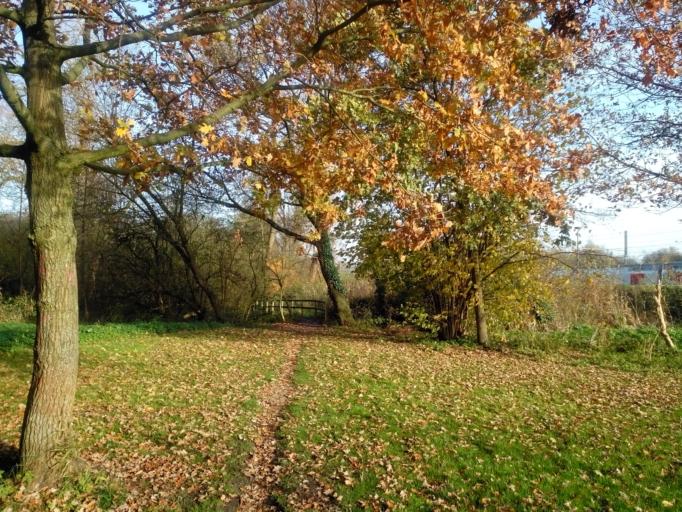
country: BE
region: Flanders
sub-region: Provincie Antwerpen
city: Turnhout
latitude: 51.3283
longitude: 4.9402
